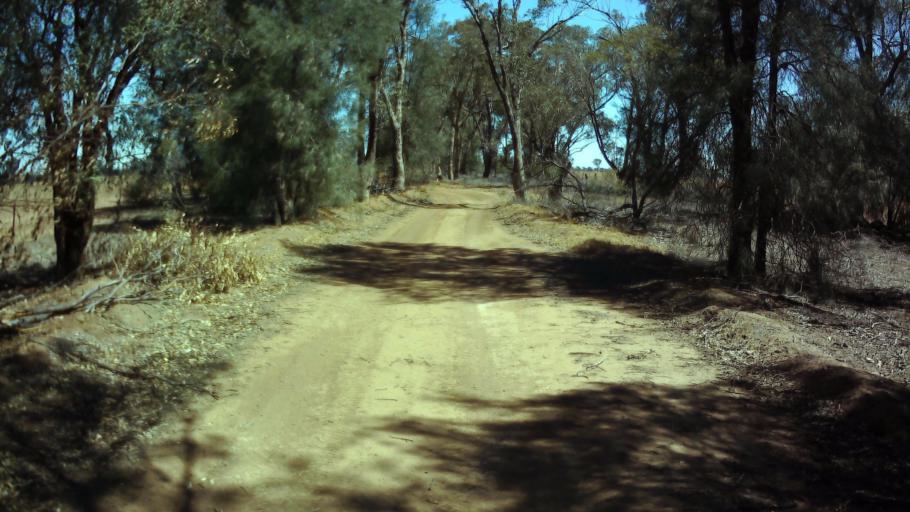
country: AU
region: New South Wales
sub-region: Bland
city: West Wyalong
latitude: -33.9151
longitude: 147.6838
